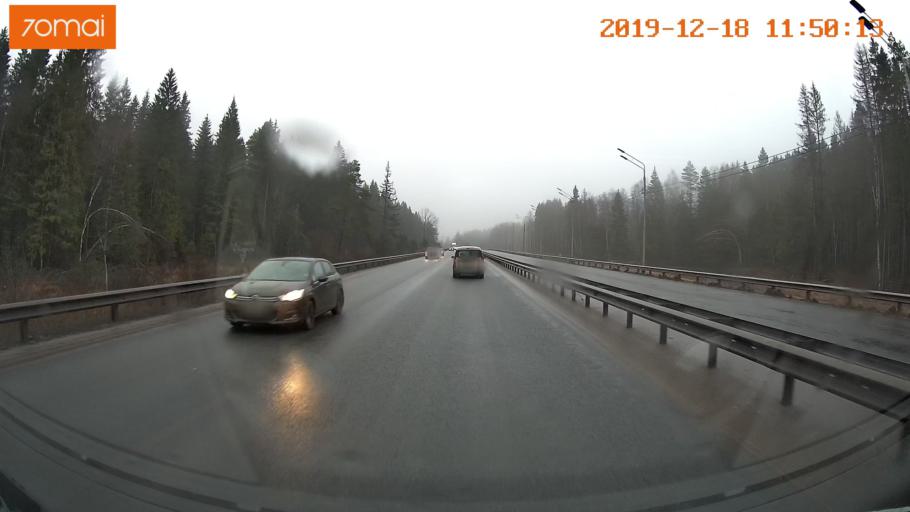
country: RU
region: Moskovskaya
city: Yershovo
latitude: 55.7840
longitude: 36.9172
